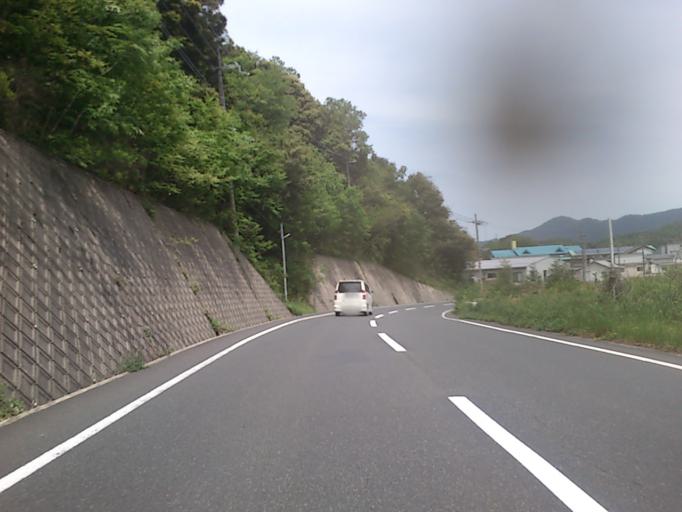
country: JP
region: Kyoto
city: Miyazu
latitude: 35.6489
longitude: 135.0849
